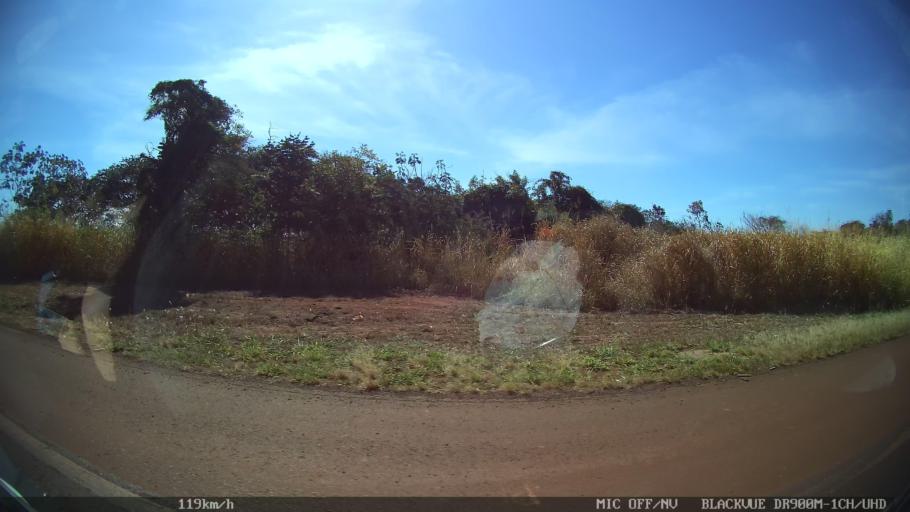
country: BR
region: Sao Paulo
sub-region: Guaira
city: Guaira
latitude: -20.4473
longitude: -48.2053
